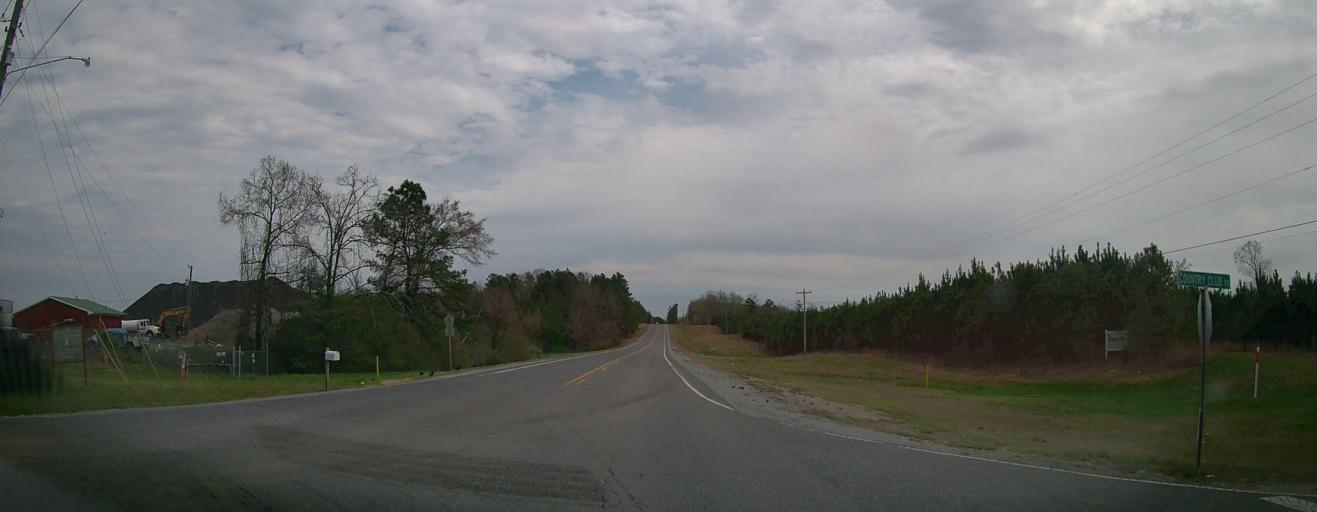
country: US
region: Alabama
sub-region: Marion County
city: Guin
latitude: 34.0383
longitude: -87.9507
